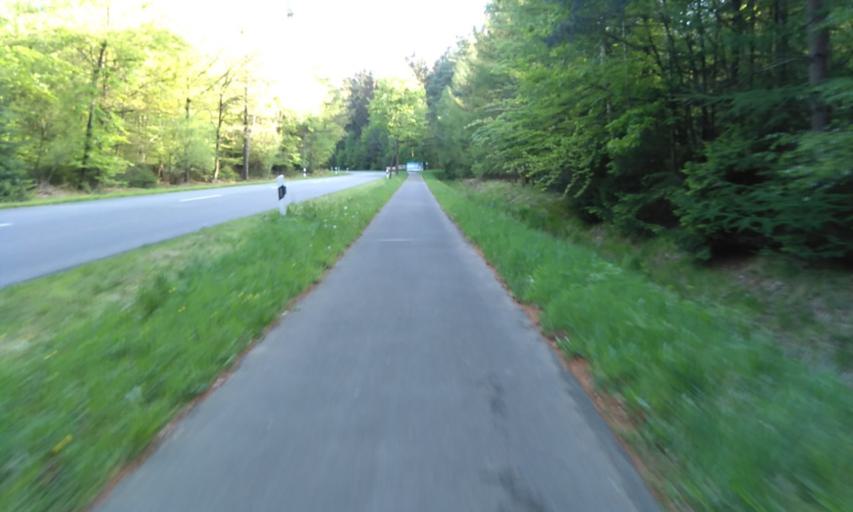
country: DE
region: Lower Saxony
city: Wohnste
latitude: 53.3990
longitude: 9.5397
